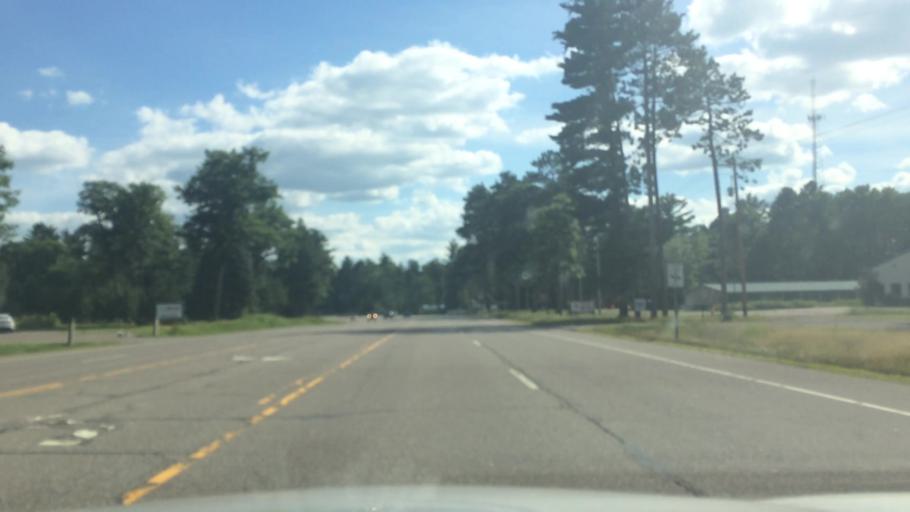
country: US
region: Wisconsin
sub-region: Vilas County
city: Lac du Flambeau
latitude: 45.8225
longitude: -89.7242
